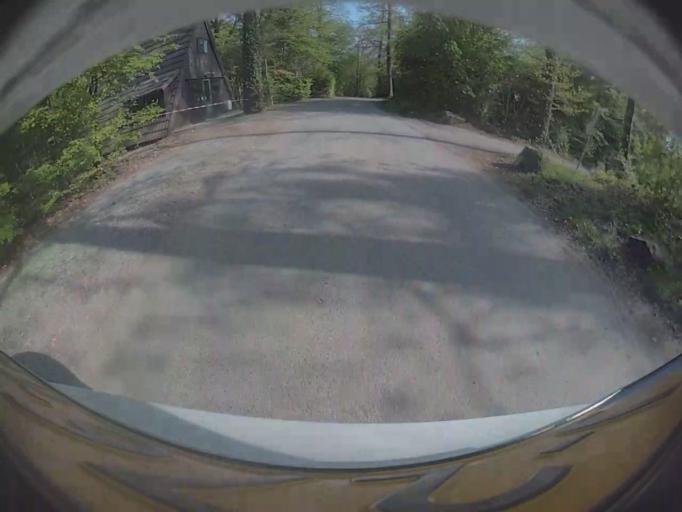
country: BE
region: Wallonia
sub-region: Province du Luxembourg
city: Durbuy
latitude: 50.3466
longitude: 5.4282
